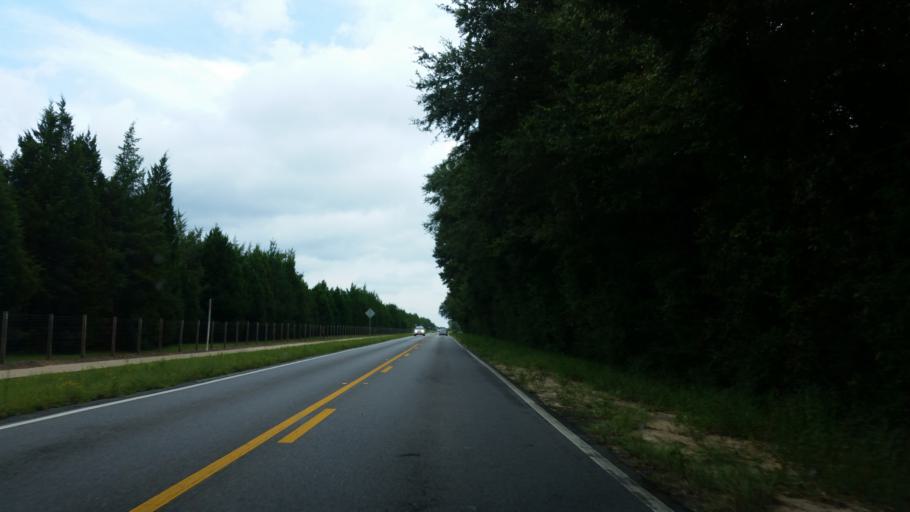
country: US
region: Florida
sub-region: Santa Rosa County
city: Pace
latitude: 30.6315
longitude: -87.1480
